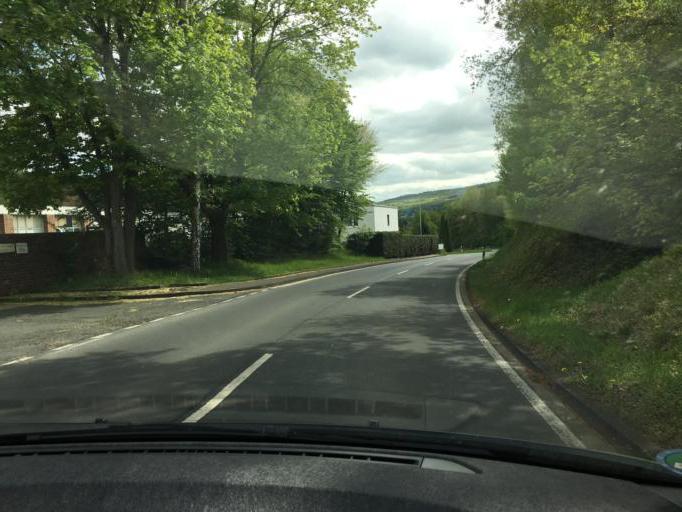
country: DE
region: North Rhine-Westphalia
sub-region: Regierungsbezirk Koln
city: Bad Munstereifel
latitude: 50.5841
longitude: 6.7620
